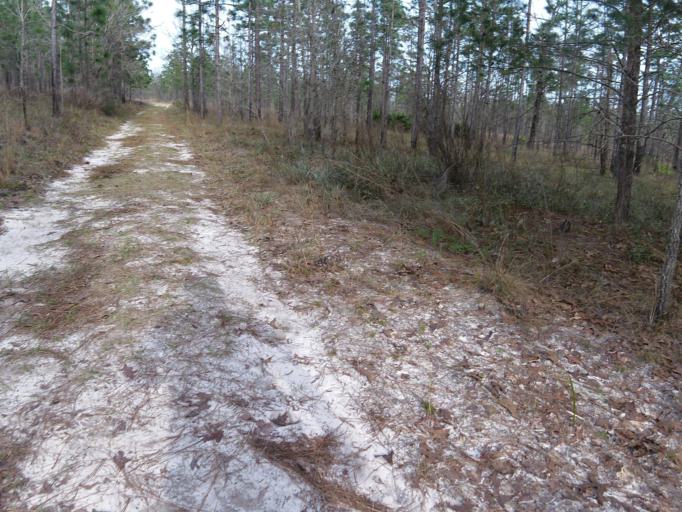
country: US
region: Florida
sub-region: Clay County
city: Middleburg
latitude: 30.1209
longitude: -81.8919
